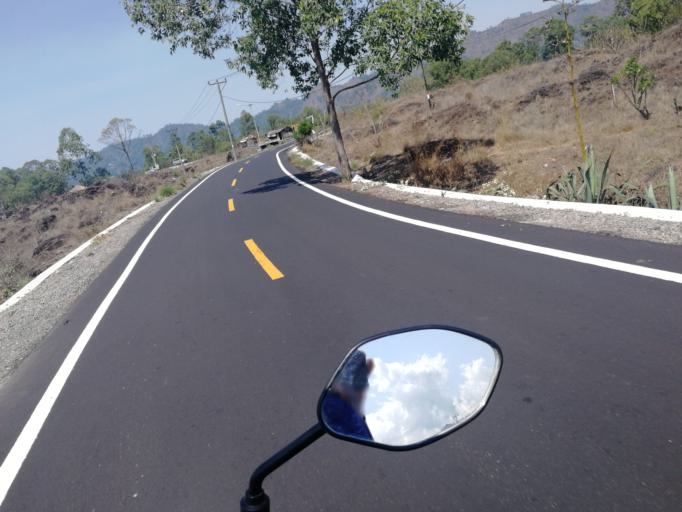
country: ID
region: Bali
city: Banjar Kedisan
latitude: -8.2552
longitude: 115.3954
